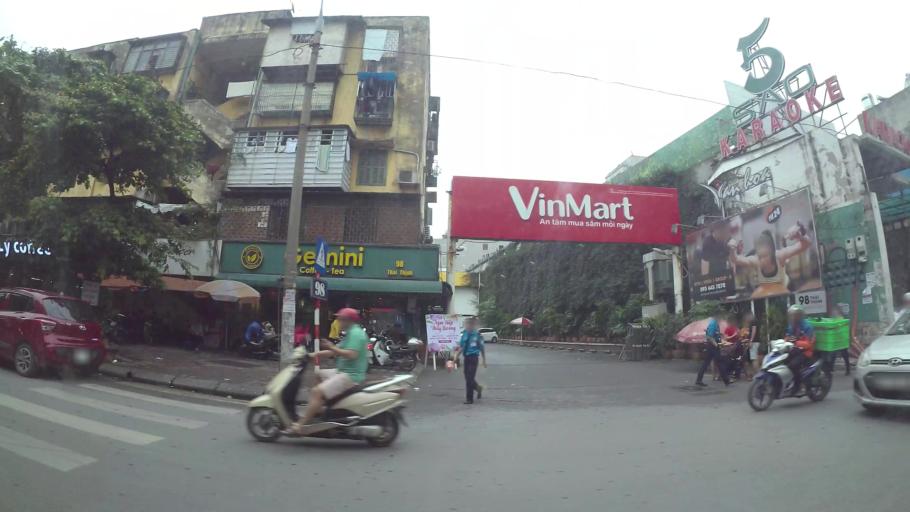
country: VN
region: Ha Noi
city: Dong Da
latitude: 21.0073
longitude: 105.8211
